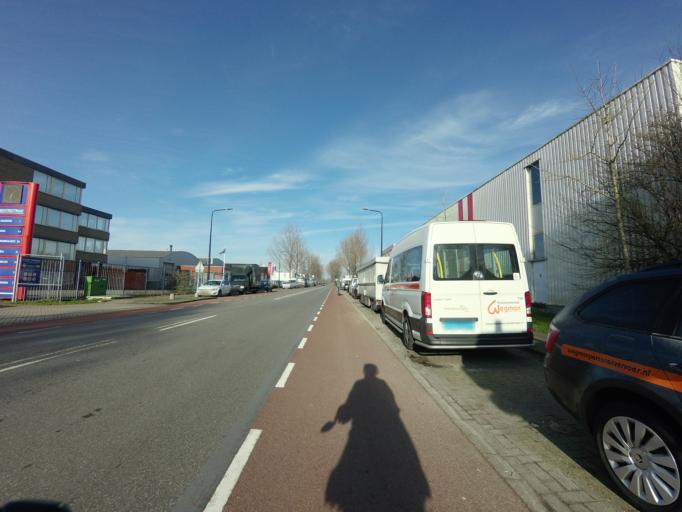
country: NL
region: South Holland
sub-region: Gemeente Gouda
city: Gouda
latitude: 52.0112
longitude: 4.6935
